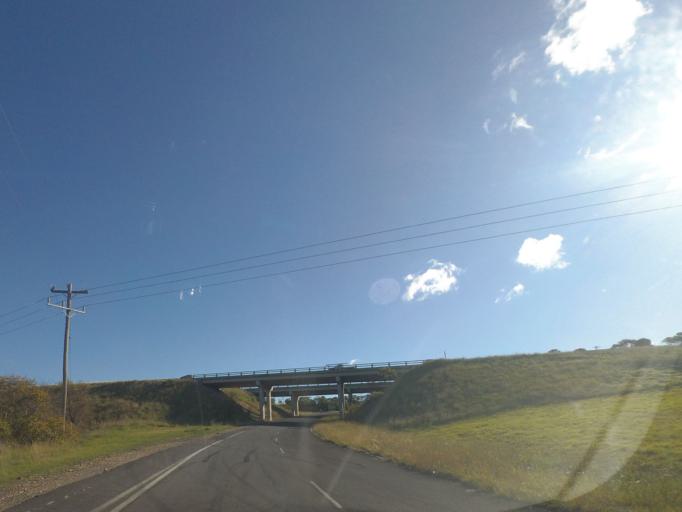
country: AU
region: Victoria
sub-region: Moorabool
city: Bacchus Marsh
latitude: -37.6651
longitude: 144.3873
